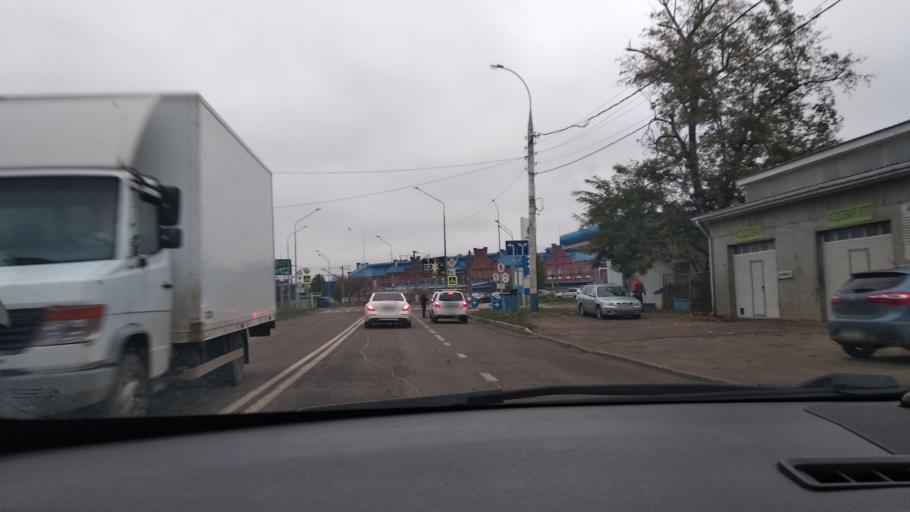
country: RU
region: Krasnodarskiy
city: Krasnodar
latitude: 45.0286
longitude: 39.0168
